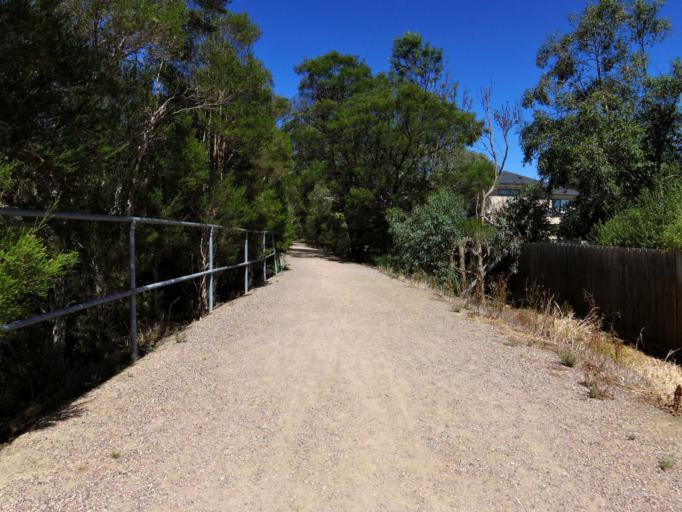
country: AU
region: Victoria
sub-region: Maroondah
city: Croydon North
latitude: -37.7743
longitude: 145.3015
